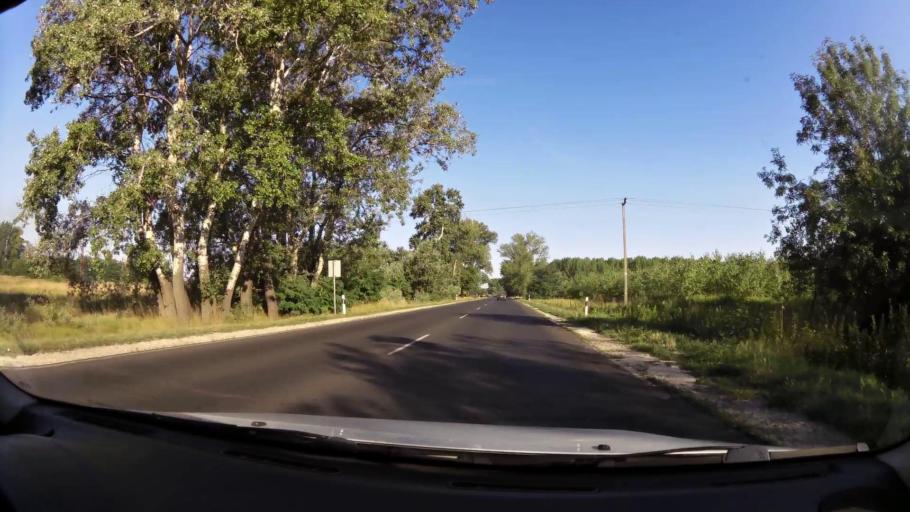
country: HU
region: Pest
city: Monor
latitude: 47.3241
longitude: 19.4644
